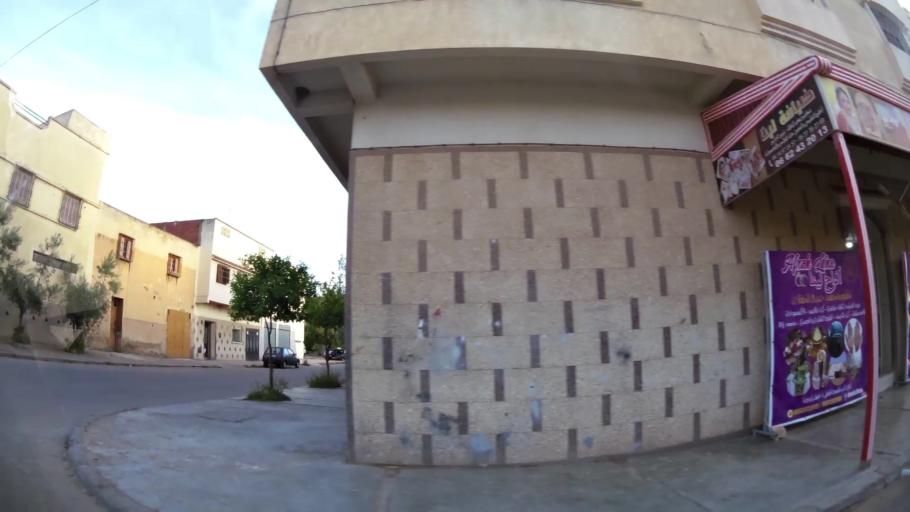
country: MA
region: Oriental
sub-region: Oujda-Angad
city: Oujda
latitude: 34.6790
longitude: -1.8833
